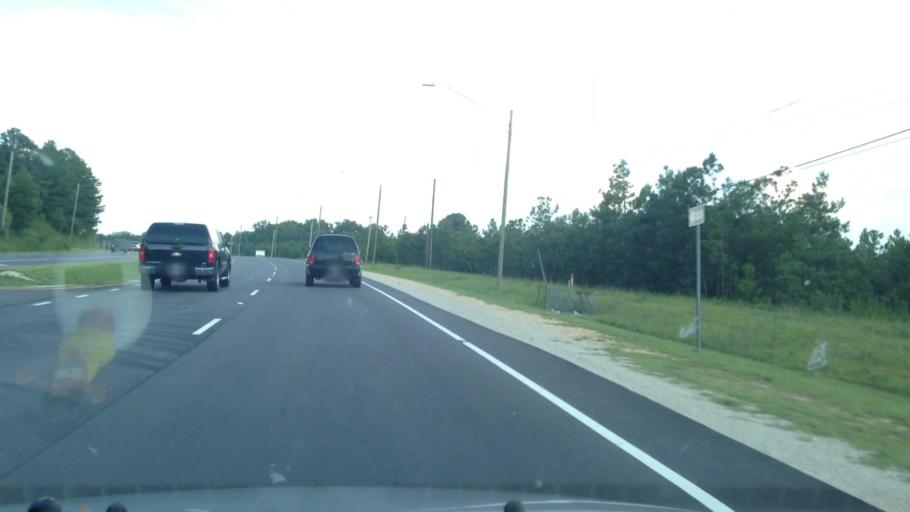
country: US
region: North Carolina
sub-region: Harnett County
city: Lillington
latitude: 35.4116
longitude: -78.7918
